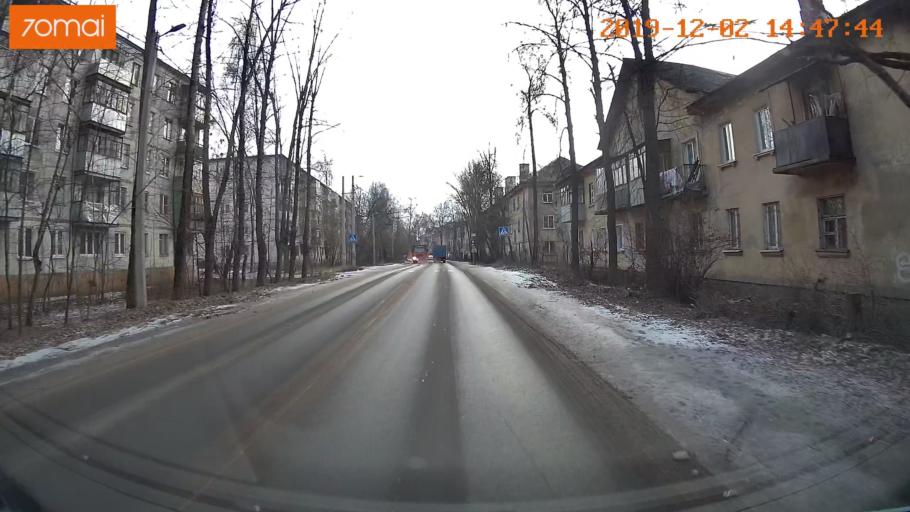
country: RU
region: Ivanovo
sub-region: Gorod Ivanovo
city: Ivanovo
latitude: 56.9878
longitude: 41.0175
